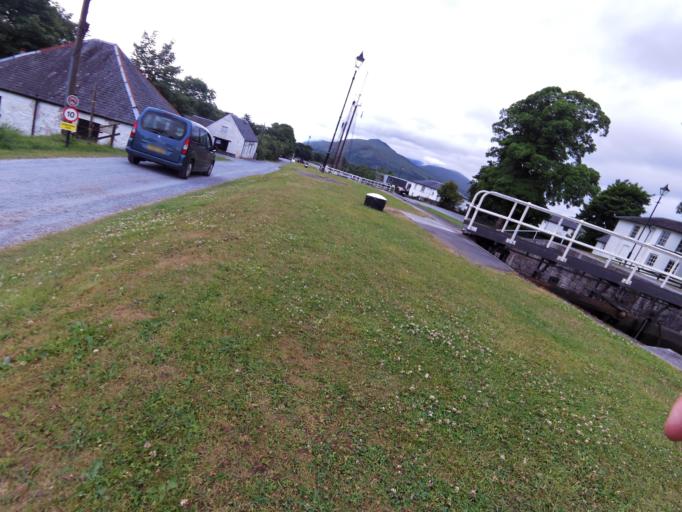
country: GB
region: Scotland
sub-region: Highland
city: Fort William
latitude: 56.8466
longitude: -5.0932
